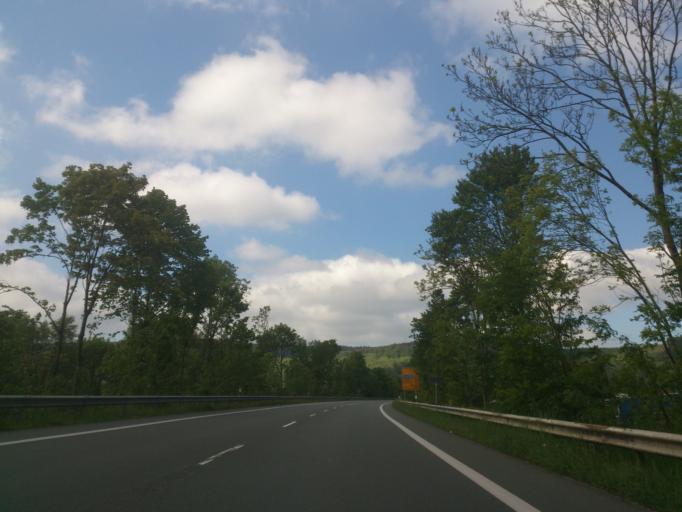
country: DE
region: North Rhine-Westphalia
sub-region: Regierungsbezirk Detmold
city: Bad Driburg
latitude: 51.7216
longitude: 9.0219
